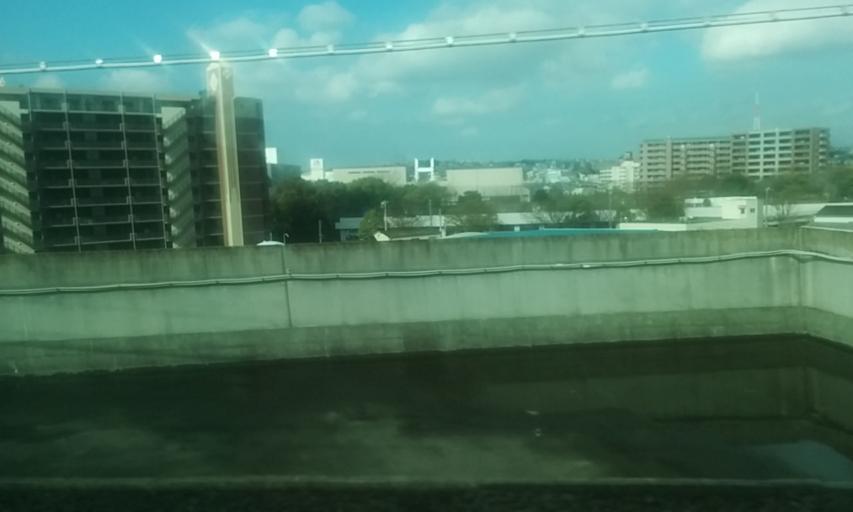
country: JP
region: Kanagawa
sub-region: Kawasaki-shi
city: Kawasaki
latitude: 35.5205
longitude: 139.6814
